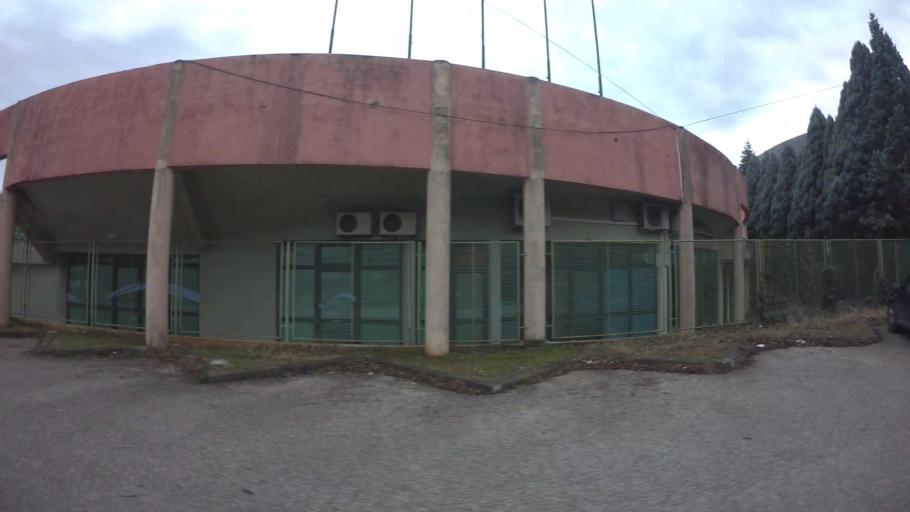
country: BA
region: Federation of Bosnia and Herzegovina
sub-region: Hercegovacko-Bosanski Kanton
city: Mostar
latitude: 43.3397
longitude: 17.8046
